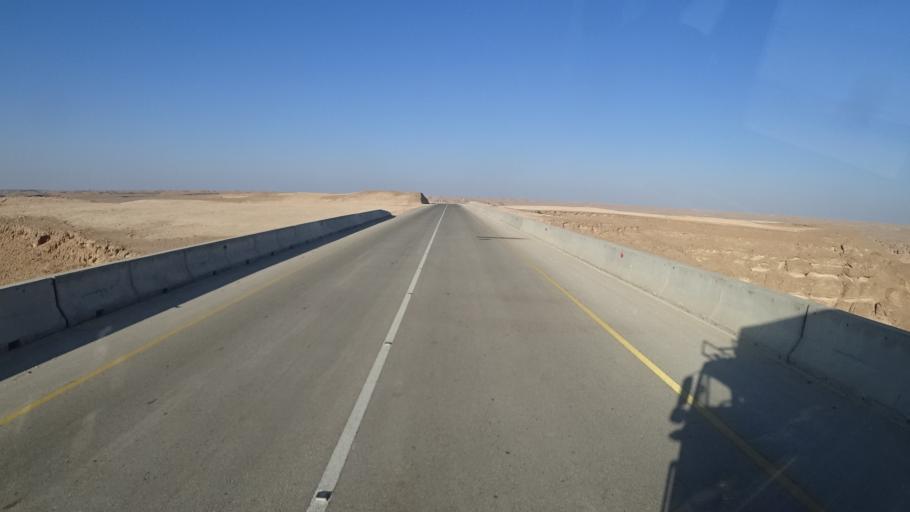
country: YE
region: Al Mahrah
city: Hawf
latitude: 17.0777
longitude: 53.0310
